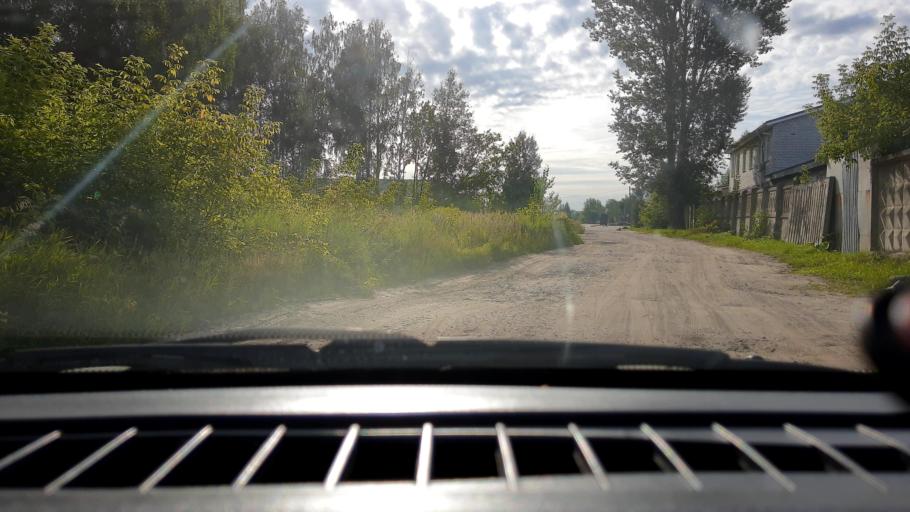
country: RU
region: Nizjnij Novgorod
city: Gorbatovka
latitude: 56.3545
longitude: 43.7897
